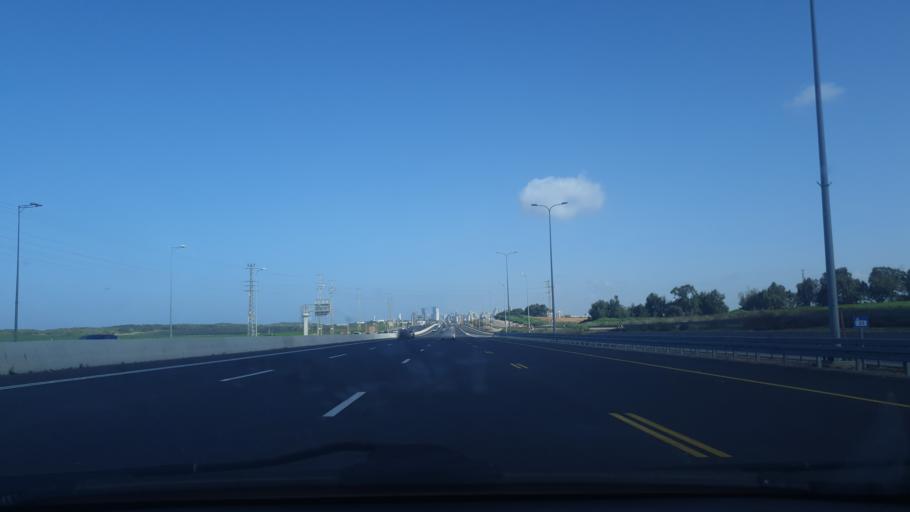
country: IL
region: Tel Aviv
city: Kefar Shemaryahu
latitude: 32.2358
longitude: 34.8329
